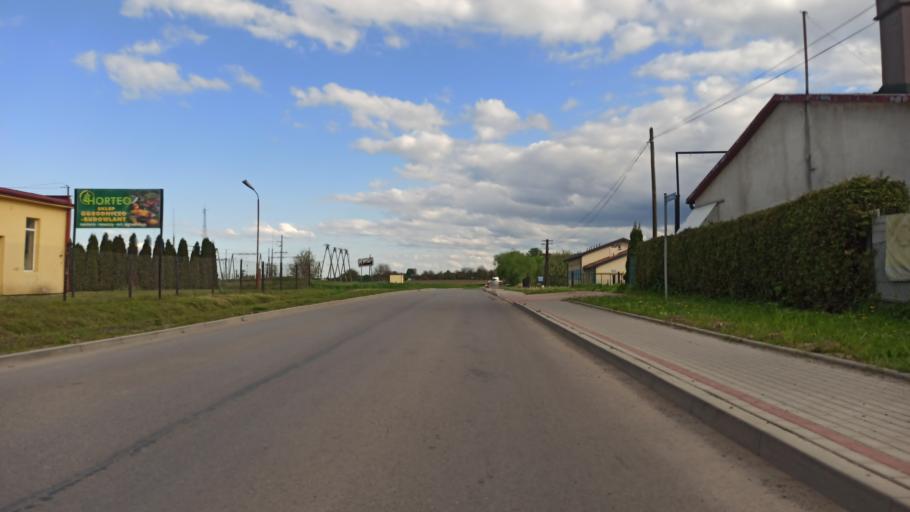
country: PL
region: Subcarpathian Voivodeship
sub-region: Powiat jaroslawski
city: Radymno
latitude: 49.9375
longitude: 22.8355
